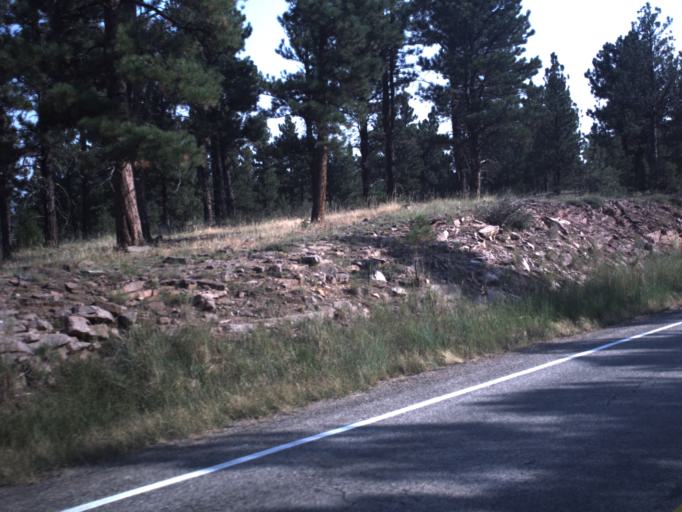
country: US
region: Utah
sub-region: Daggett County
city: Manila
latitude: 40.8674
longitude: -109.4746
